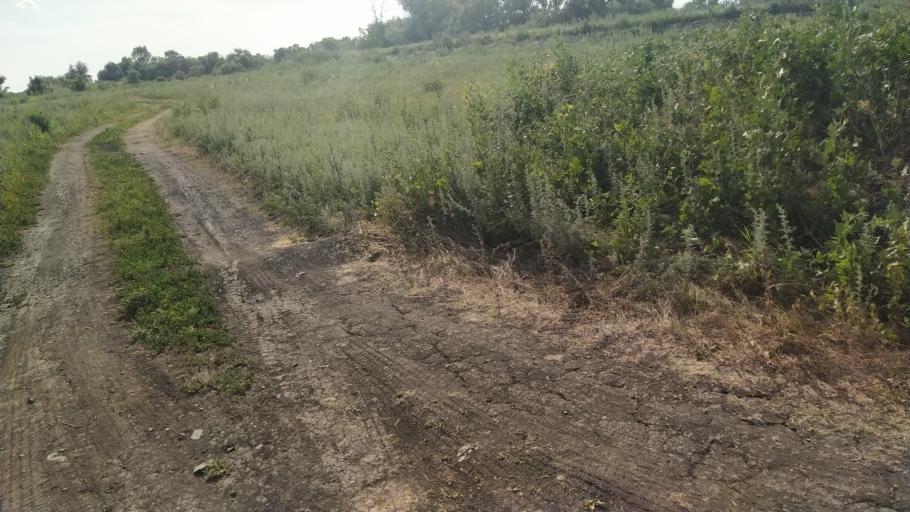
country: RU
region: Rostov
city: Kuleshovka
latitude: 47.1278
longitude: 39.6111
